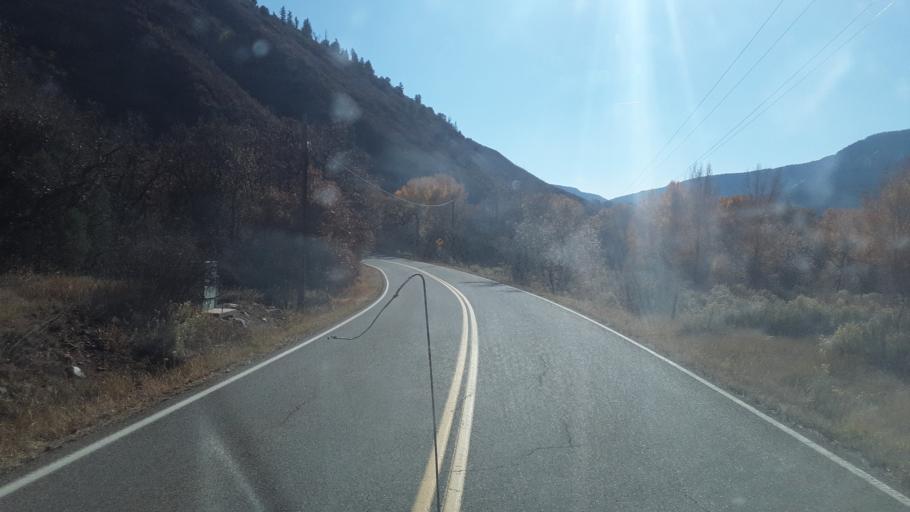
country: US
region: Colorado
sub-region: La Plata County
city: Durango
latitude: 37.3938
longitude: -107.8240
